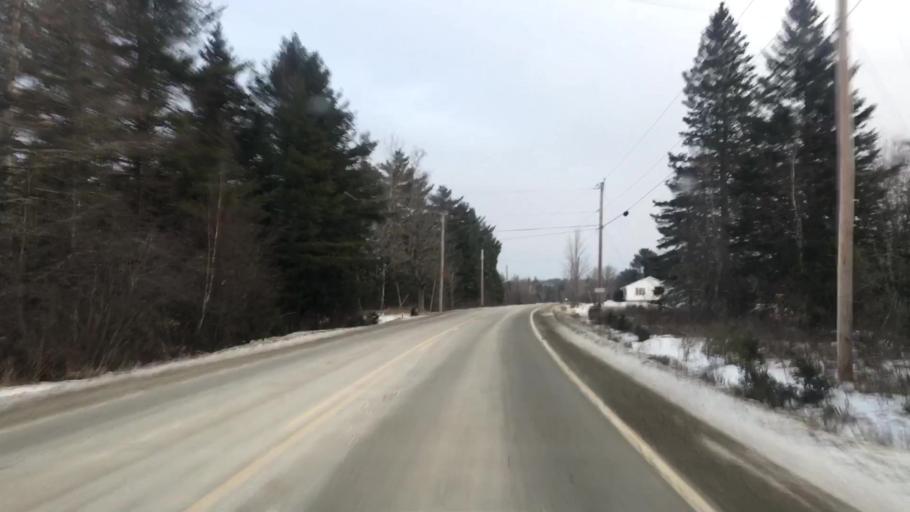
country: US
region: Maine
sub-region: Hancock County
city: Franklin
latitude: 44.6901
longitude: -68.3486
